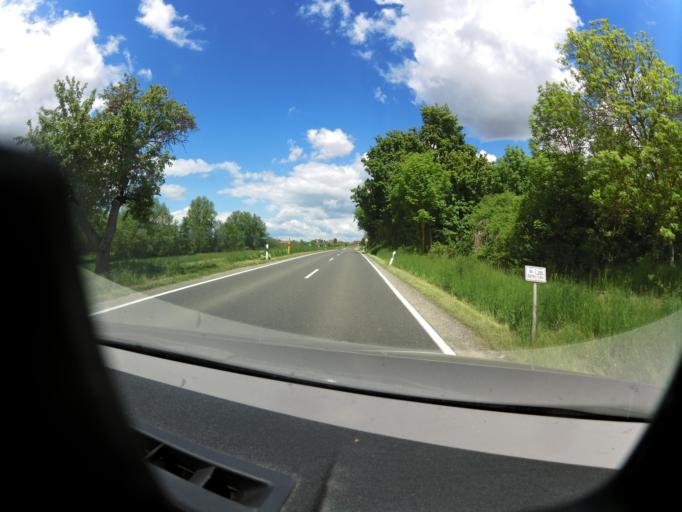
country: DE
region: Bavaria
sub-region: Regierungsbezirk Unterfranken
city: Prosselsheim
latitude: 49.8723
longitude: 10.1264
